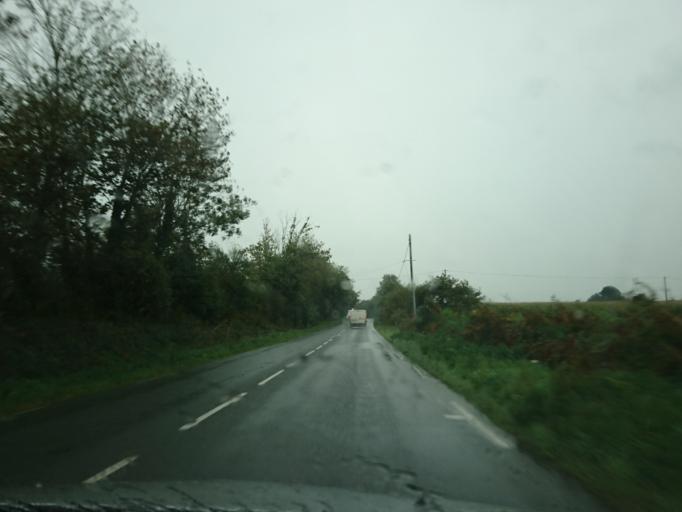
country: FR
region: Brittany
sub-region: Departement du Finistere
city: Plabennec
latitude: 48.4843
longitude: -4.4353
